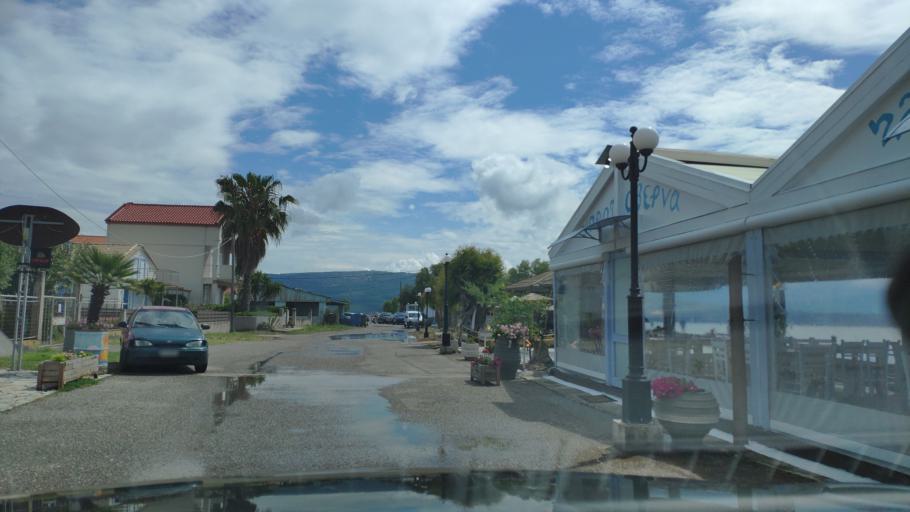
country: GR
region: West Greece
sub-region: Nomos Aitolias kai Akarnanias
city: Krikellos
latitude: 38.9286
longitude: 21.1407
